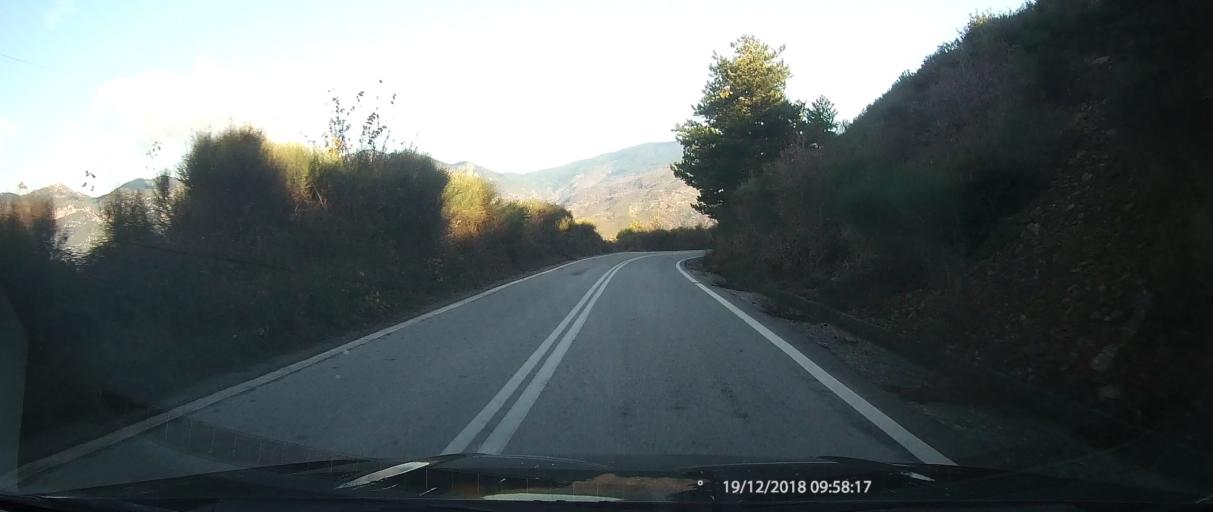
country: GR
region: Peloponnese
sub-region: Nomos Messinias
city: Paralia Vergas
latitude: 37.0898
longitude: 22.2363
